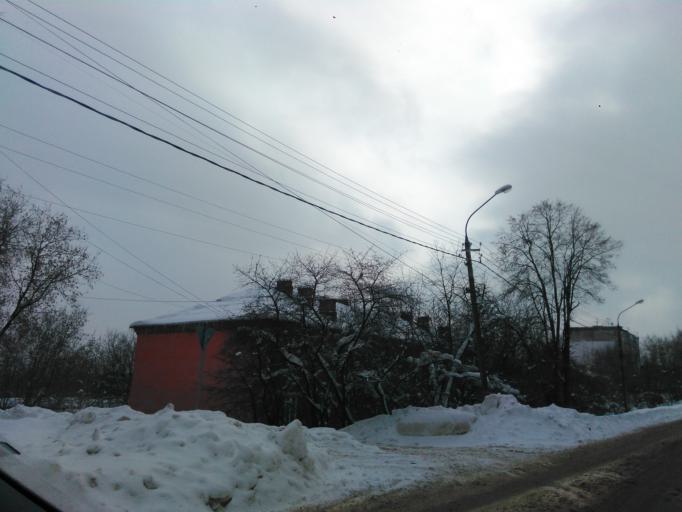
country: RU
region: Moskovskaya
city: Yakhroma
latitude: 56.2781
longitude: 37.4835
